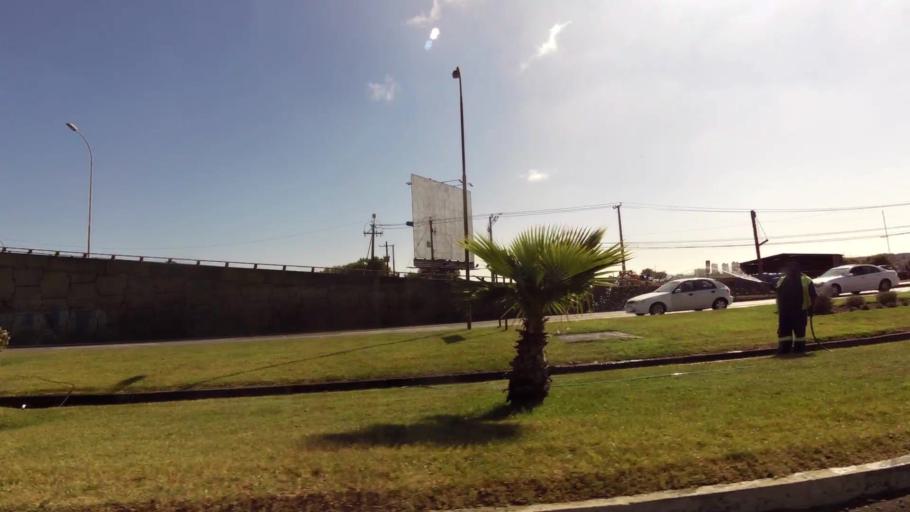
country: CL
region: Biobio
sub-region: Provincia de Concepcion
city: Concepcion
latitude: -36.7900
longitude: -73.0712
